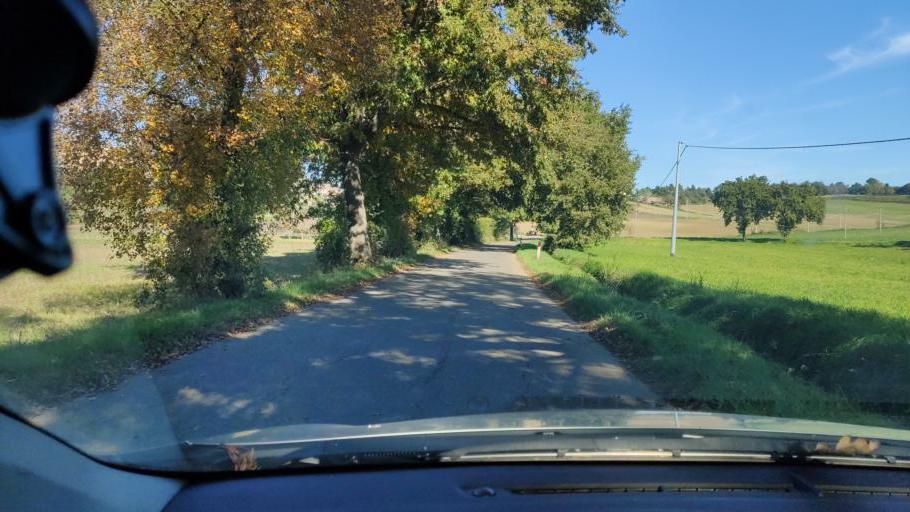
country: IT
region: Umbria
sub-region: Provincia di Terni
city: Amelia
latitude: 42.5932
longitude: 12.4359
